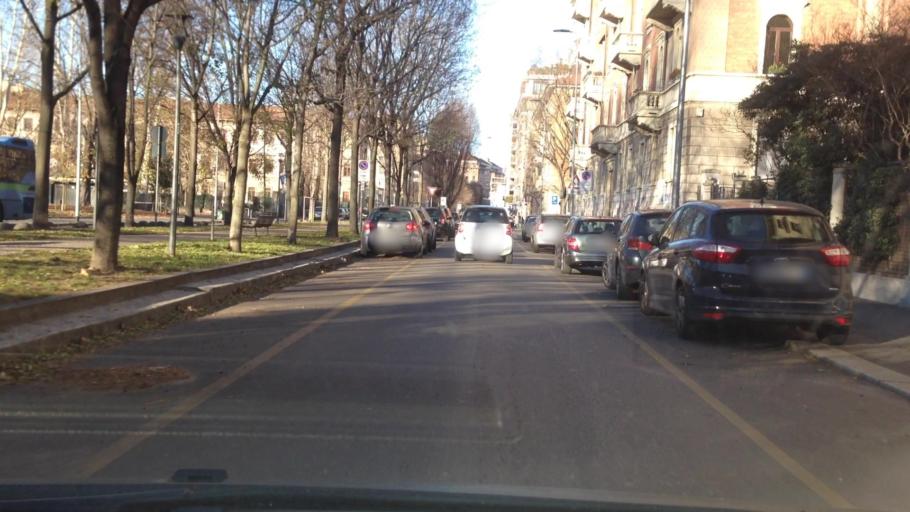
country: IT
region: Lombardy
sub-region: Citta metropolitana di Milano
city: Milano
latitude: 45.4477
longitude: 9.1943
